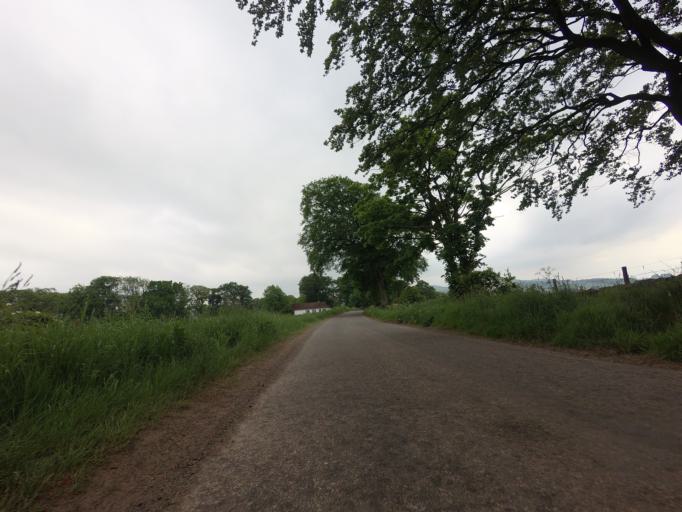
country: GB
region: Scotland
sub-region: Perth and Kinross
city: Kinross
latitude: 56.1753
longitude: -3.4391
